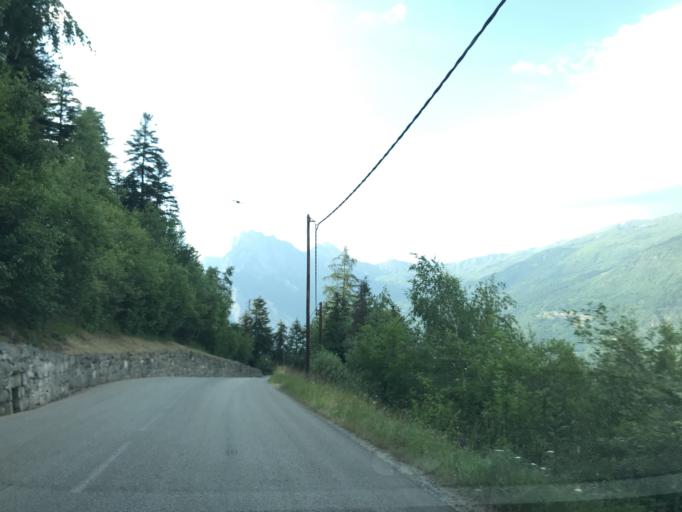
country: FR
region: Rhone-Alpes
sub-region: Departement de la Savoie
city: Saint-Michel-de-Maurienne
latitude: 45.1998
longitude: 6.4679
